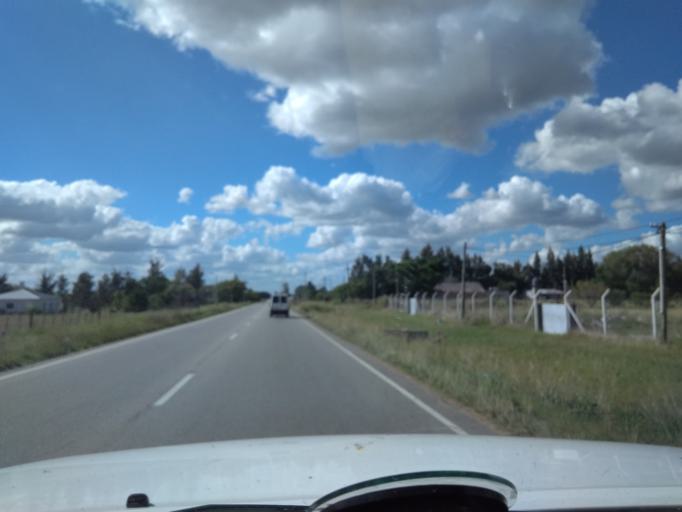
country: UY
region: Canelones
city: Sauce
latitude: -34.6843
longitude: -56.0531
